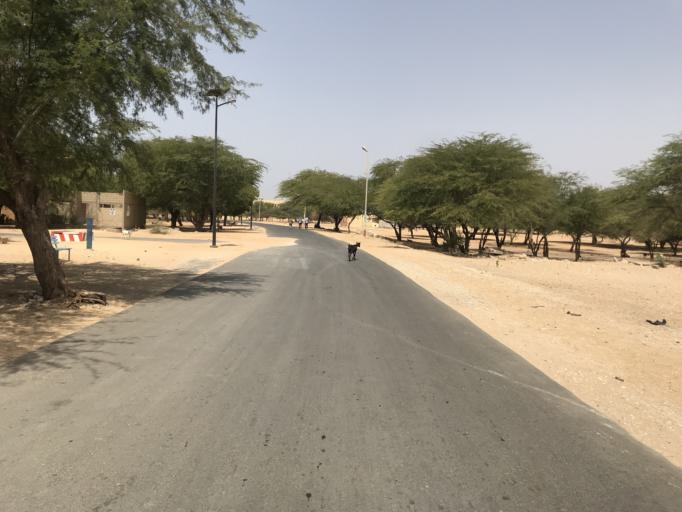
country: SN
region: Saint-Louis
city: Saint-Louis
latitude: 16.0661
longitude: -16.4204
